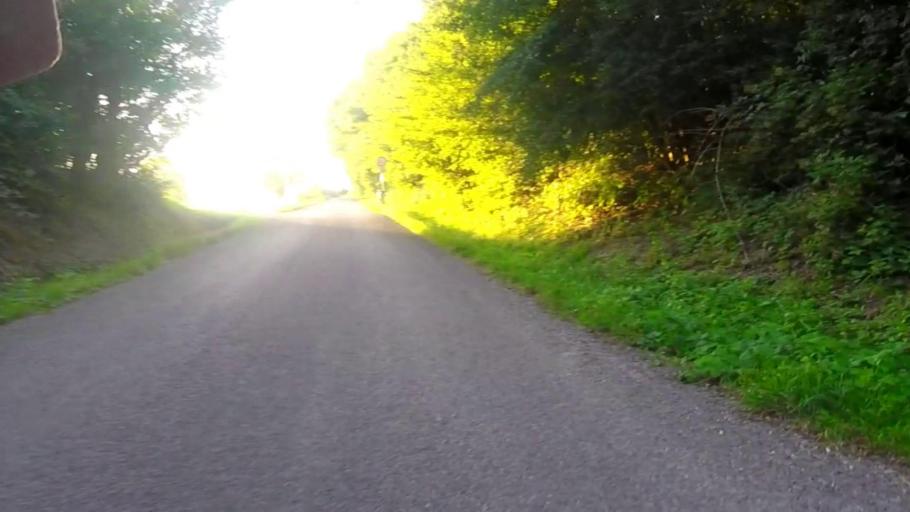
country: DE
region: Baden-Wuerttemberg
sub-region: Regierungsbezirk Stuttgart
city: Oppenweiler
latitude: 48.9948
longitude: 9.4612
